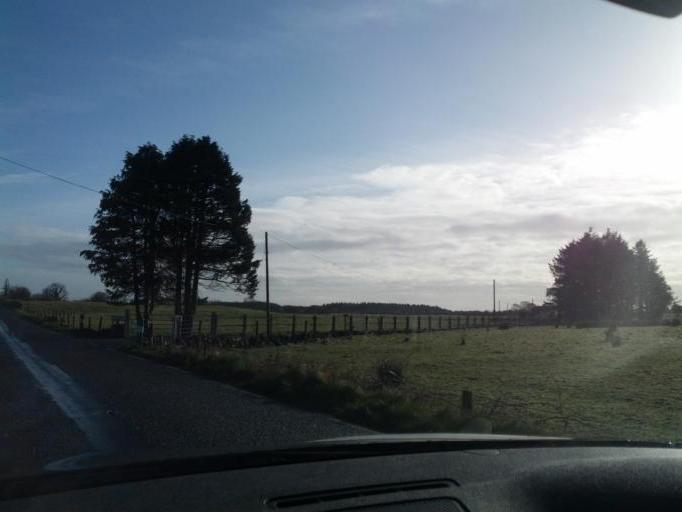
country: IE
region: Connaught
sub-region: County Galway
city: Athenry
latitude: 53.4095
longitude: -8.6310
